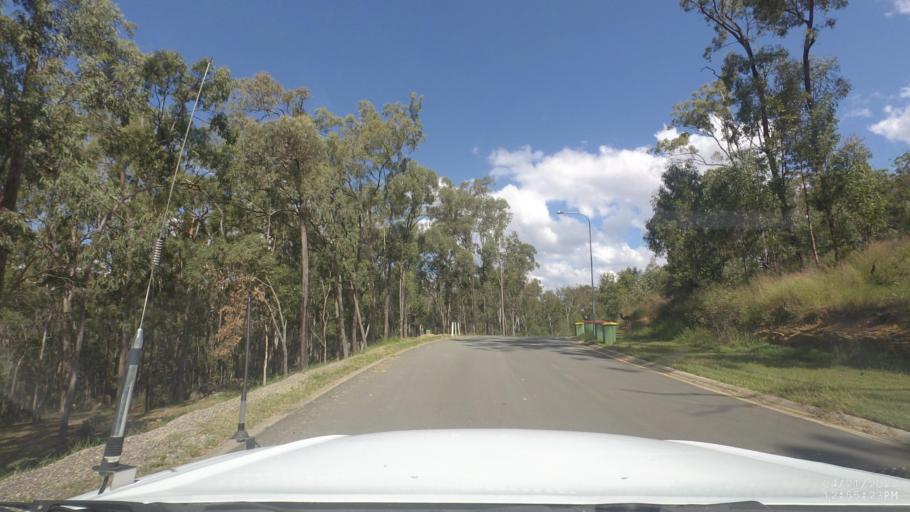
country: AU
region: Queensland
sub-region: Logan
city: Cedar Vale
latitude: -27.8358
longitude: 153.1009
